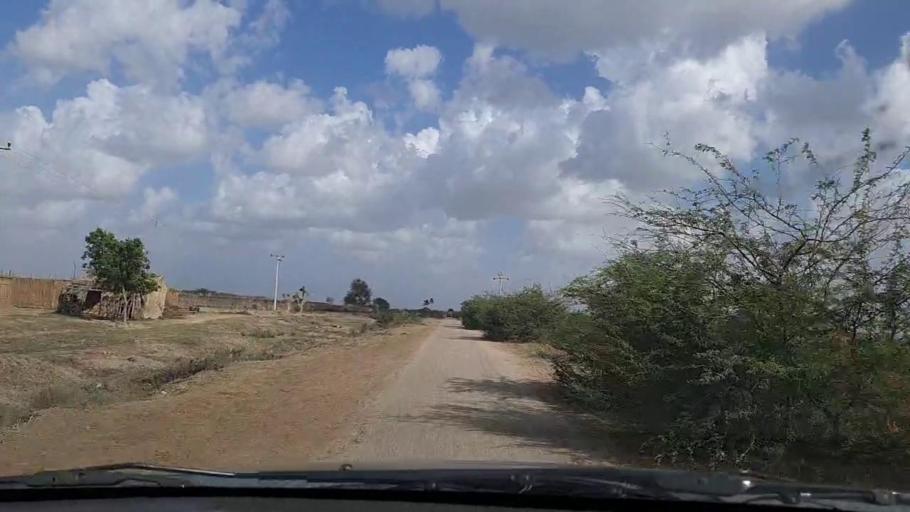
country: PK
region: Sindh
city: Keti Bandar
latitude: 24.0965
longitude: 67.6072
